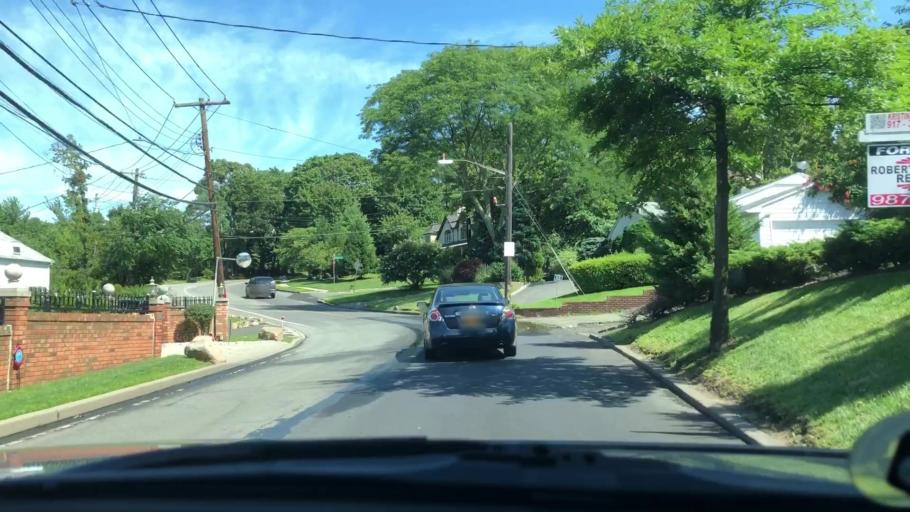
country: US
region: New York
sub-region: Richmond County
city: Staten Island
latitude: 40.5880
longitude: -74.1107
